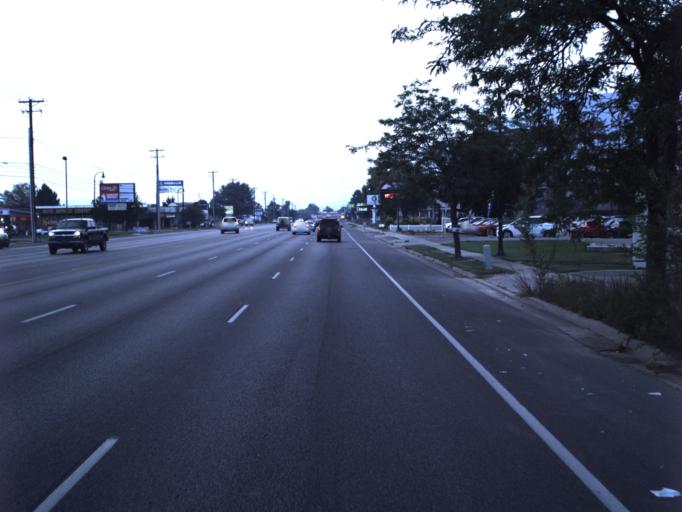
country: US
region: Utah
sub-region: Utah County
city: Orem
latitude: 40.3207
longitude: -111.7052
